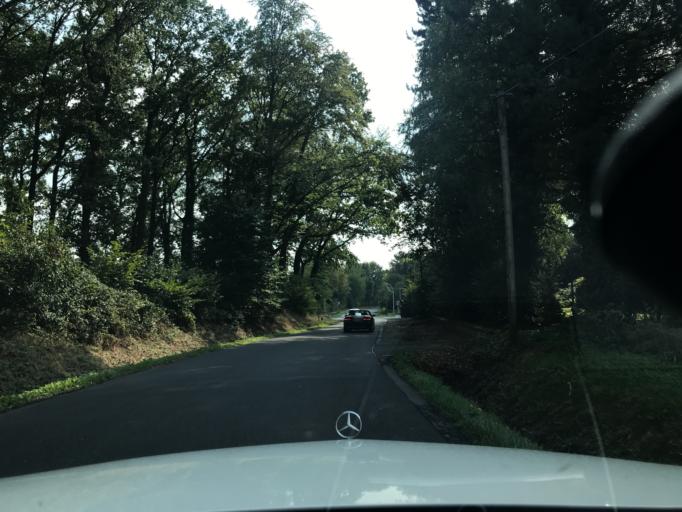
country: DE
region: North Rhine-Westphalia
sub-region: Regierungsbezirk Arnsberg
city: Werl
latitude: 51.5835
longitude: 7.8686
